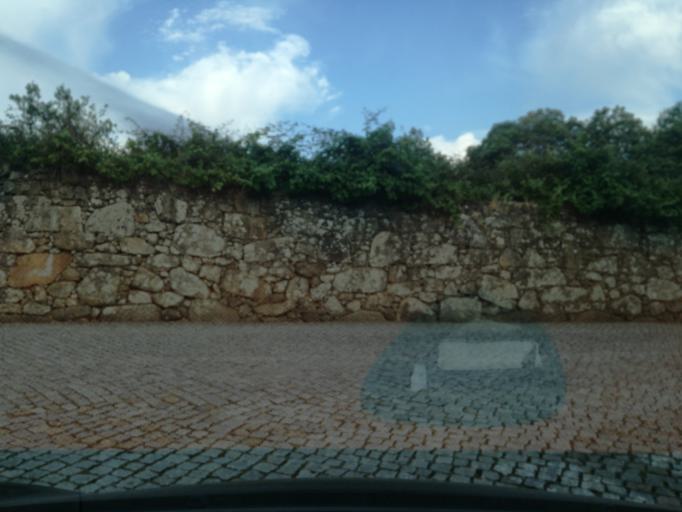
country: PT
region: Porto
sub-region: Maia
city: Nogueira
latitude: 41.2609
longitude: -8.6027
